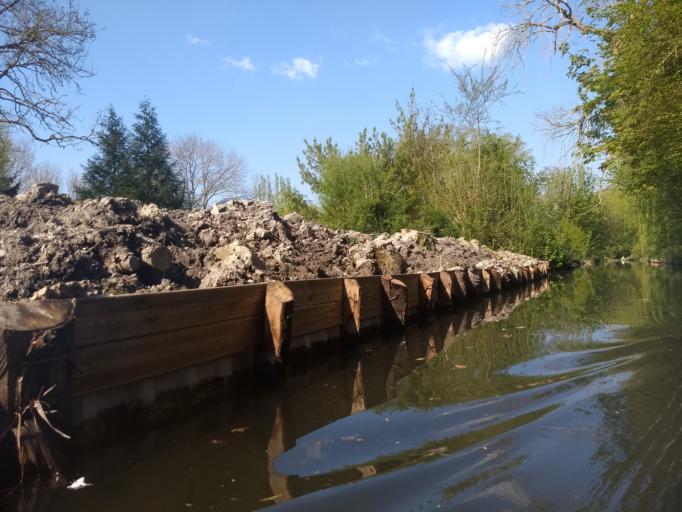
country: FR
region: Picardie
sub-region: Departement de la Somme
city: Rivery
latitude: 49.8952
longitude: 2.3256
